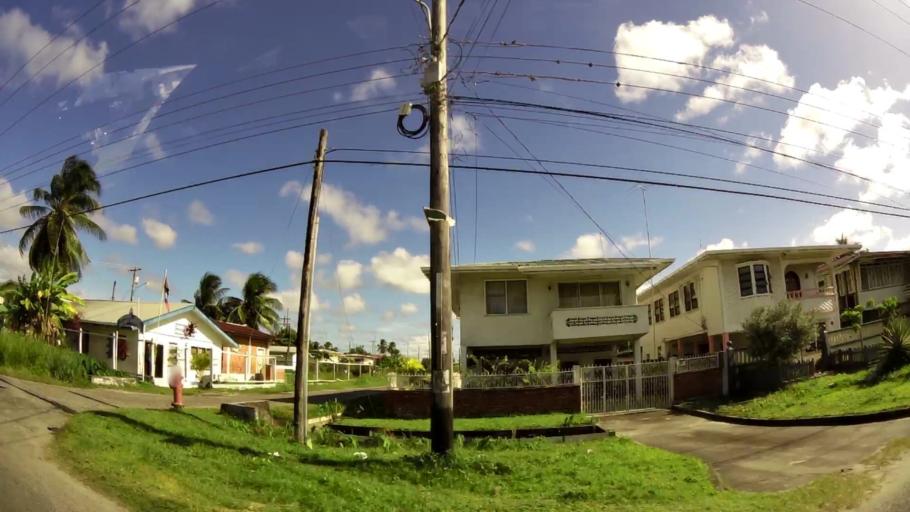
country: GY
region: Demerara-Mahaica
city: Georgetown
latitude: 6.8145
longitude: -58.1310
